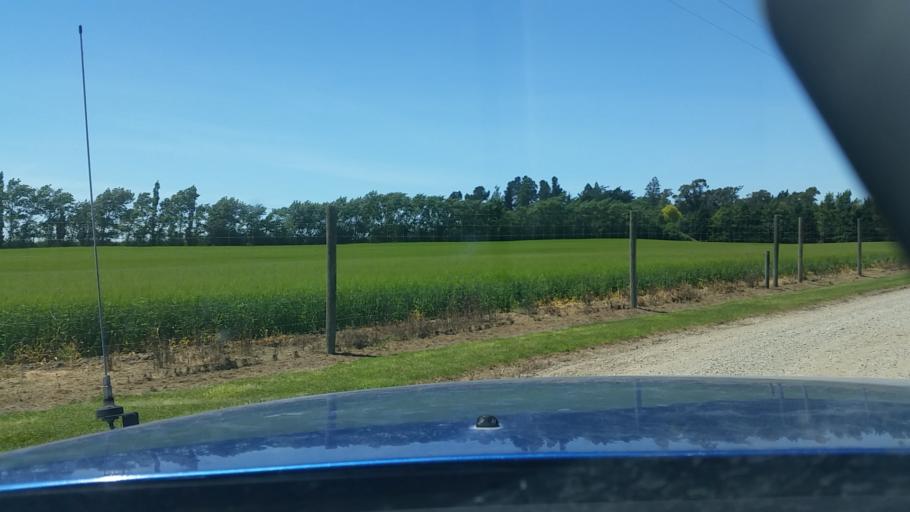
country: NZ
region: Canterbury
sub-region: Ashburton District
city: Ashburton
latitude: -43.9544
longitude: 171.8257
